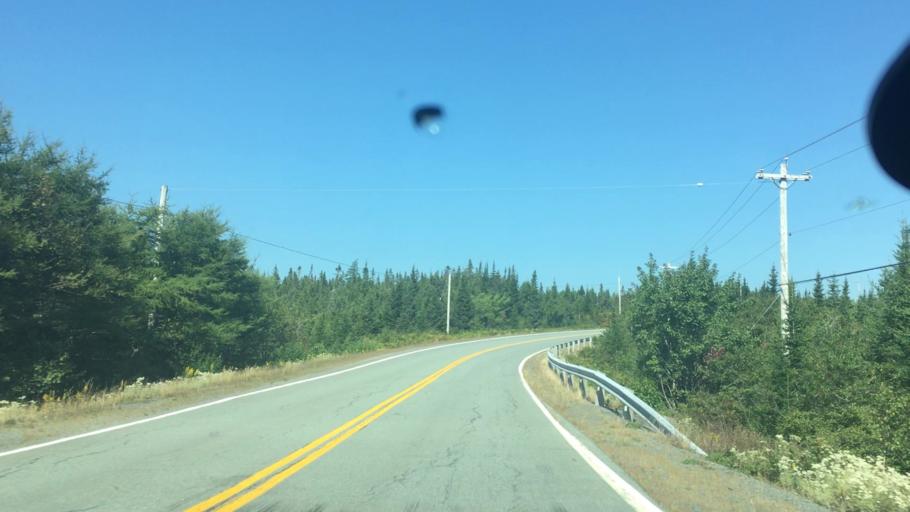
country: CA
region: Nova Scotia
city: Antigonish
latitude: 45.0073
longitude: -62.1052
